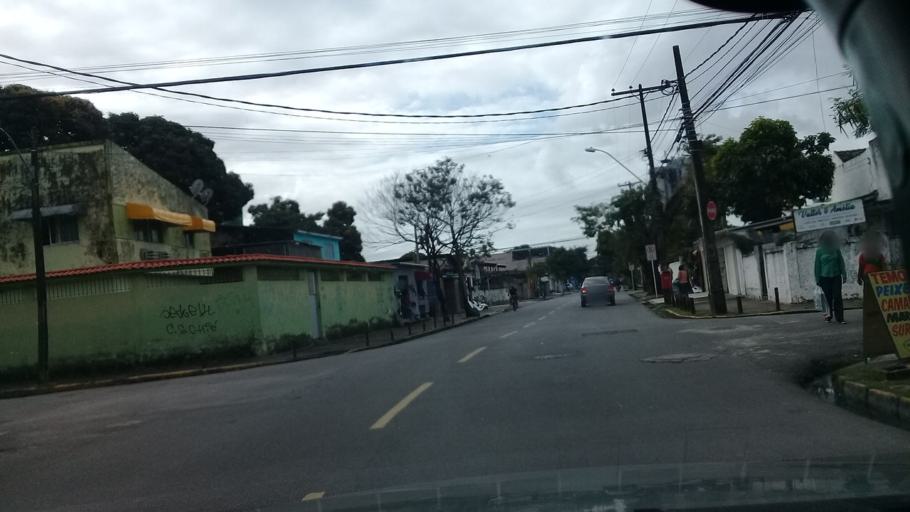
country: BR
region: Pernambuco
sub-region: Recife
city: Recife
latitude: -8.0345
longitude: -34.8808
